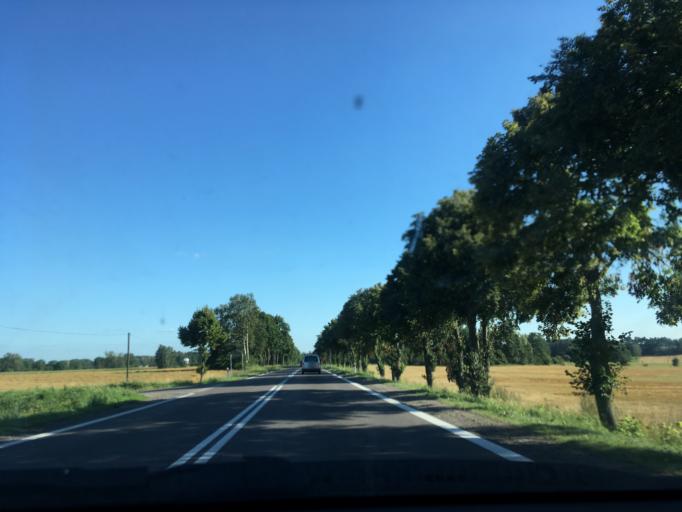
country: PL
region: Podlasie
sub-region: Powiat sokolski
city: Janow
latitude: 53.4230
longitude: 23.1093
